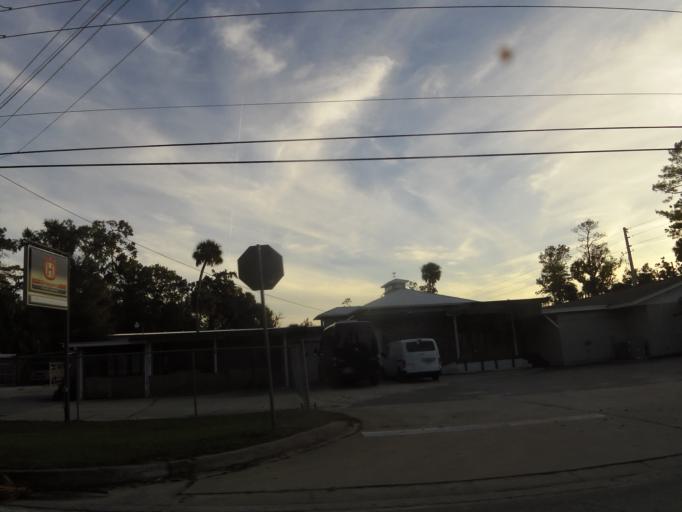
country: US
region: Florida
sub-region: Saint Johns County
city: Palm Valley
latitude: 30.1769
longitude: -81.3998
